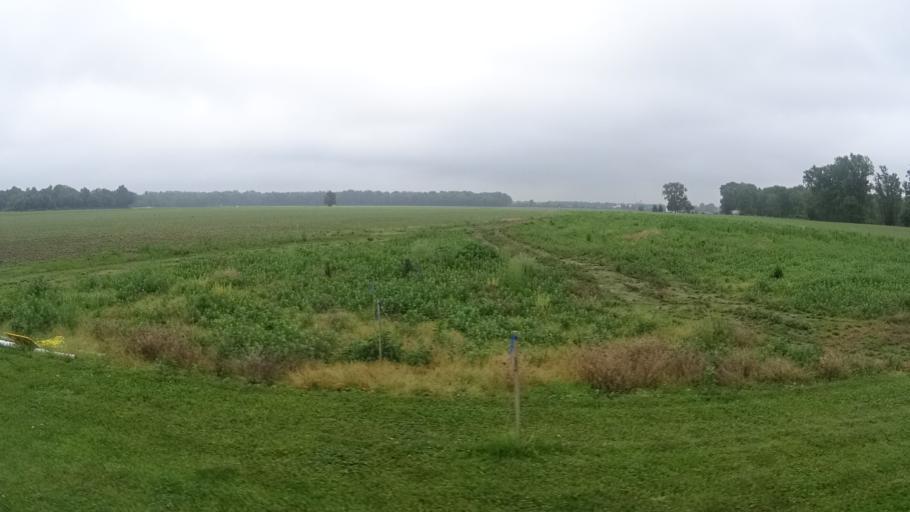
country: US
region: Ohio
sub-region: Huron County
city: Bellevue
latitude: 41.3515
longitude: -82.8169
